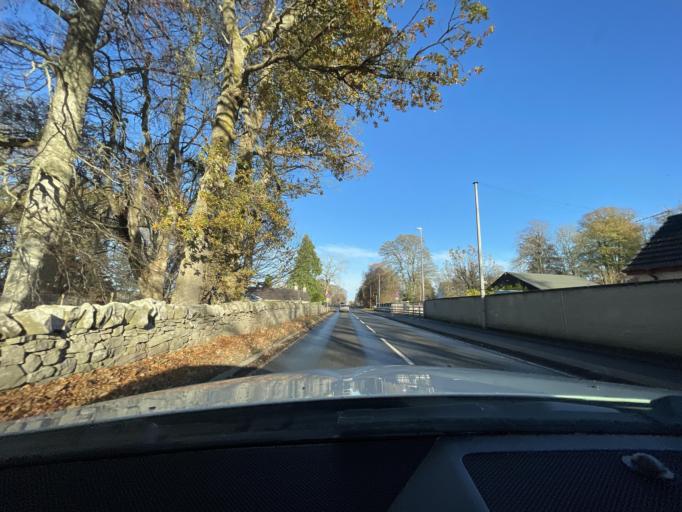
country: GB
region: Scotland
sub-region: Highland
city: Inverness
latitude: 57.4493
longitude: -4.2525
